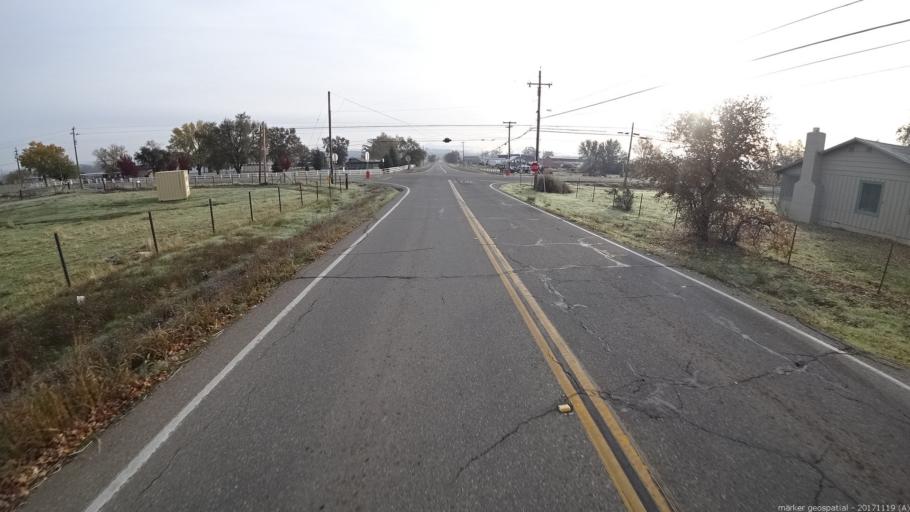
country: US
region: California
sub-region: Shasta County
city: Anderson
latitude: 40.4765
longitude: -122.2420
